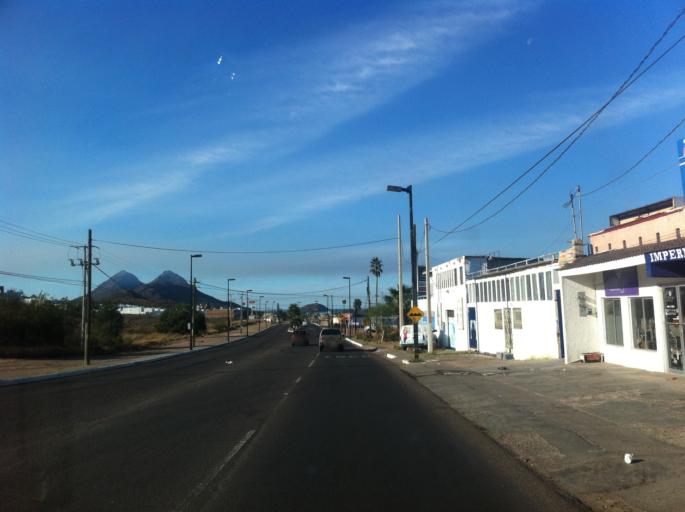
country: MX
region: Sonora
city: Heroica Guaymas
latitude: 27.9275
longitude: -110.9297
